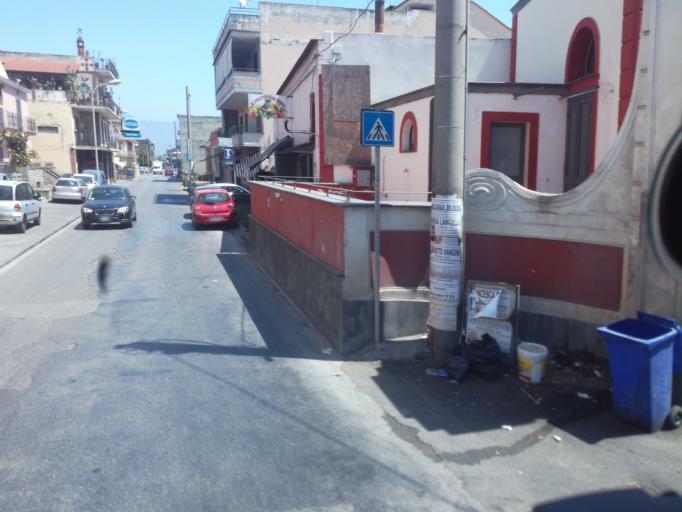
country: IT
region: Campania
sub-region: Provincia di Napoli
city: Boscoreale
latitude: 40.7833
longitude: 14.5093
